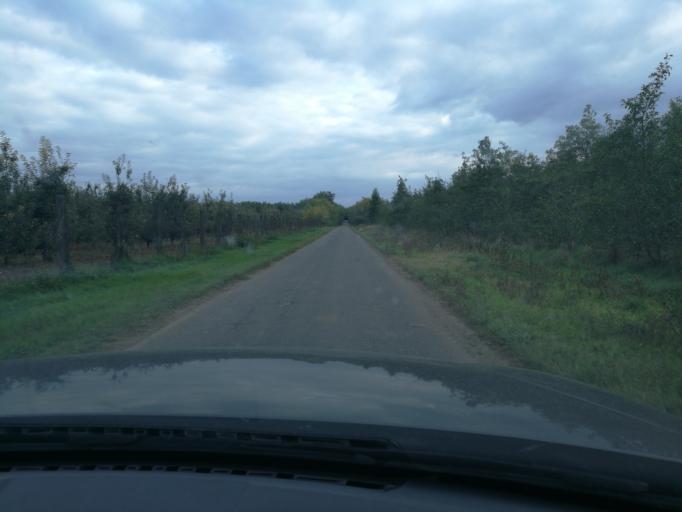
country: HU
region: Szabolcs-Szatmar-Bereg
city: Napkor
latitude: 47.9958
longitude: 21.8835
